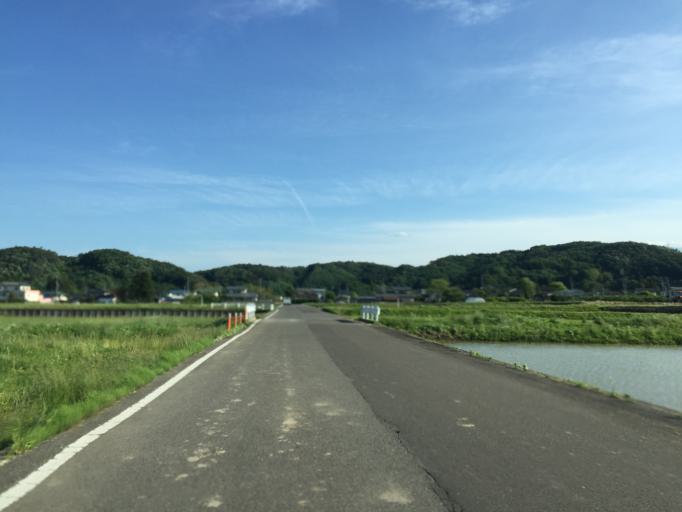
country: JP
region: Fukushima
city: Fukushima-shi
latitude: 37.7318
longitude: 140.4192
